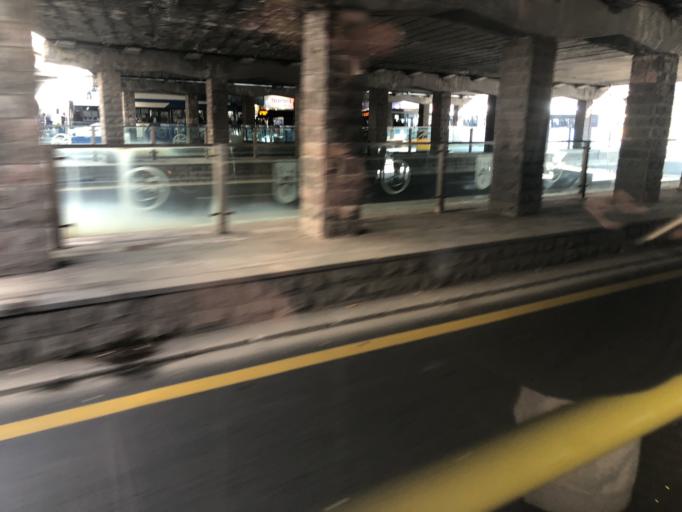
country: TR
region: Ankara
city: Ankara
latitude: 39.9293
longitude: 32.8547
